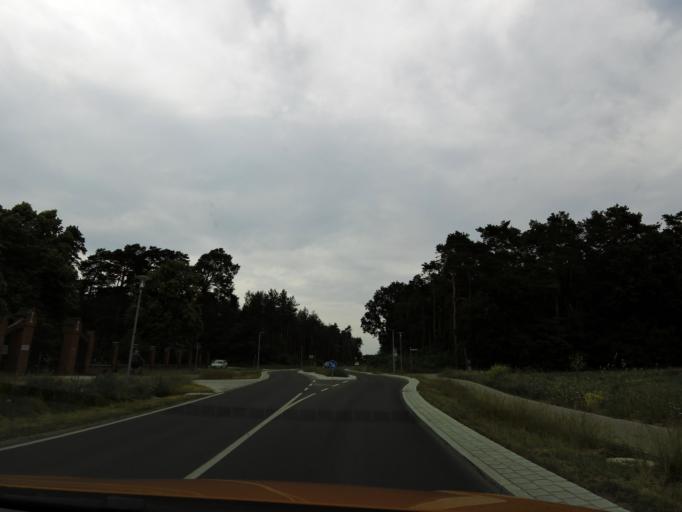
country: DE
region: Brandenburg
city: Rangsdorf
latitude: 52.3404
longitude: 13.3996
